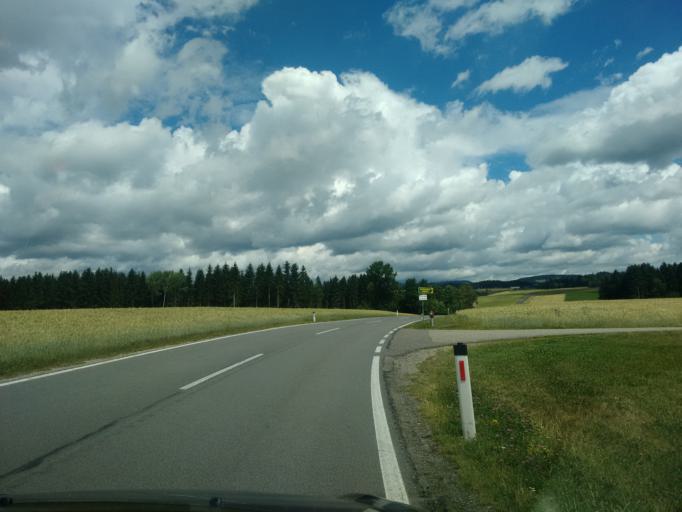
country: AT
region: Upper Austria
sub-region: Politischer Bezirk Urfahr-Umgebung
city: Gramastetten
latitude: 48.4010
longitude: 14.1804
